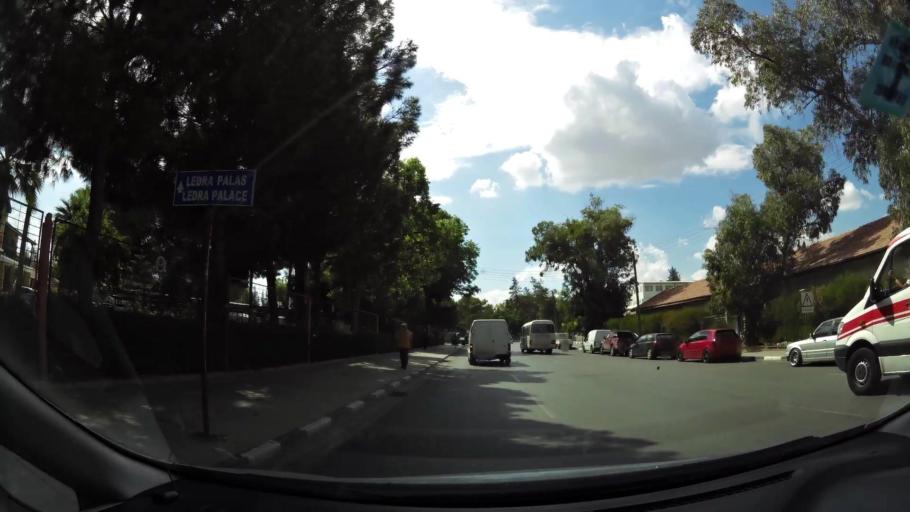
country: CY
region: Lefkosia
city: Nicosia
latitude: 35.1840
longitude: 33.3642
